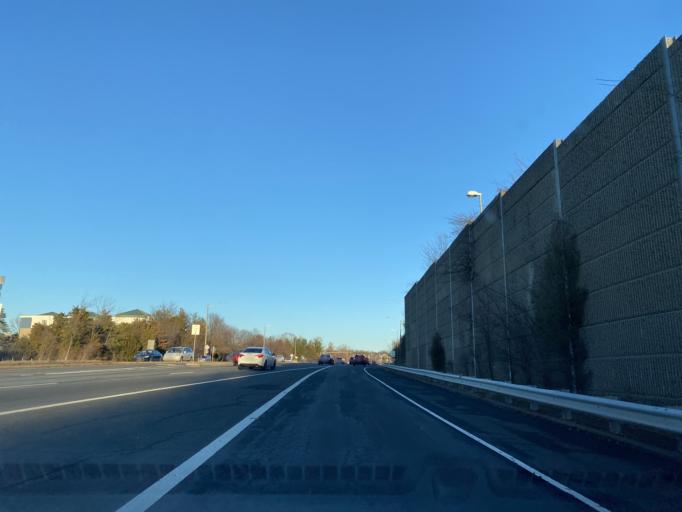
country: US
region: Virginia
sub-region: Fairfax County
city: Centreville
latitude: 38.8376
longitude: -77.4446
